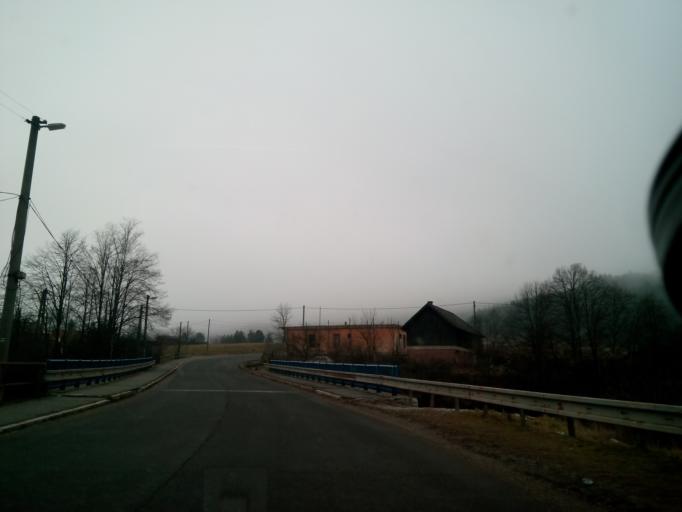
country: SK
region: Kosicky
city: Krompachy
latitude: 48.9232
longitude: 20.9321
